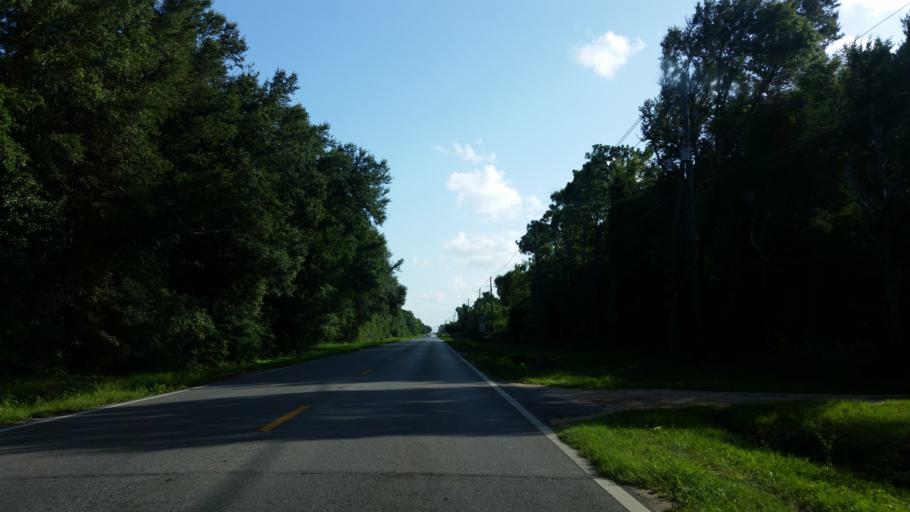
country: US
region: Florida
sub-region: Santa Rosa County
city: Bagdad
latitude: 30.5849
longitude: -87.0882
